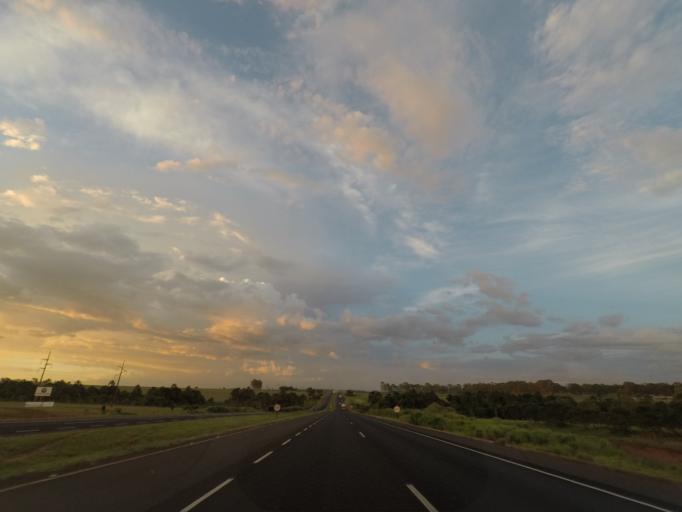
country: BR
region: Minas Gerais
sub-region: Uberaba
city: Uberaba
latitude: -19.6367
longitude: -48.0112
